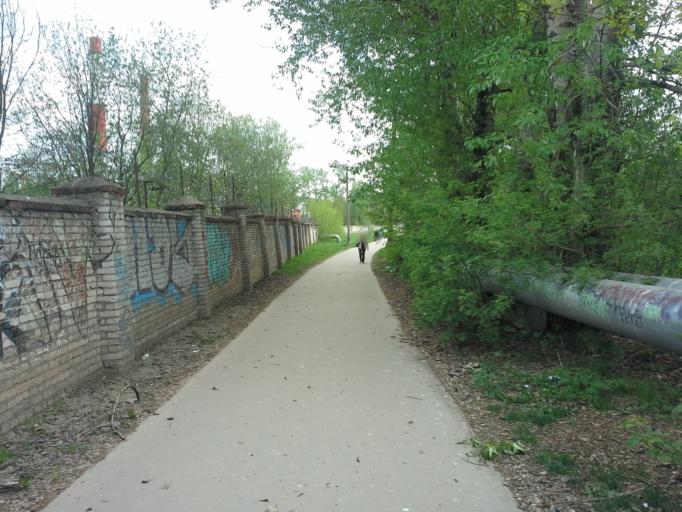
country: RU
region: Moskovskaya
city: Sergiyev Posad
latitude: 56.3184
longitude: 38.1438
